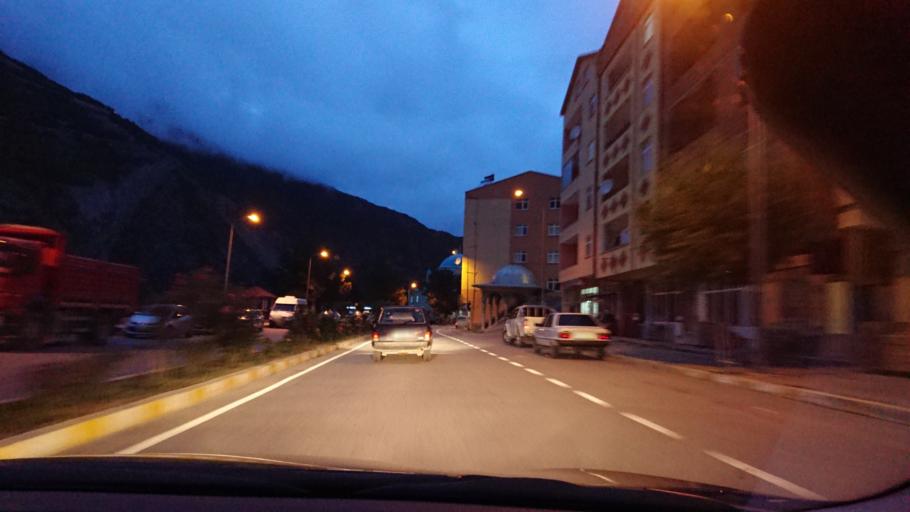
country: TR
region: Gumushane
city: Kurtun
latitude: 40.6689
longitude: 39.1405
